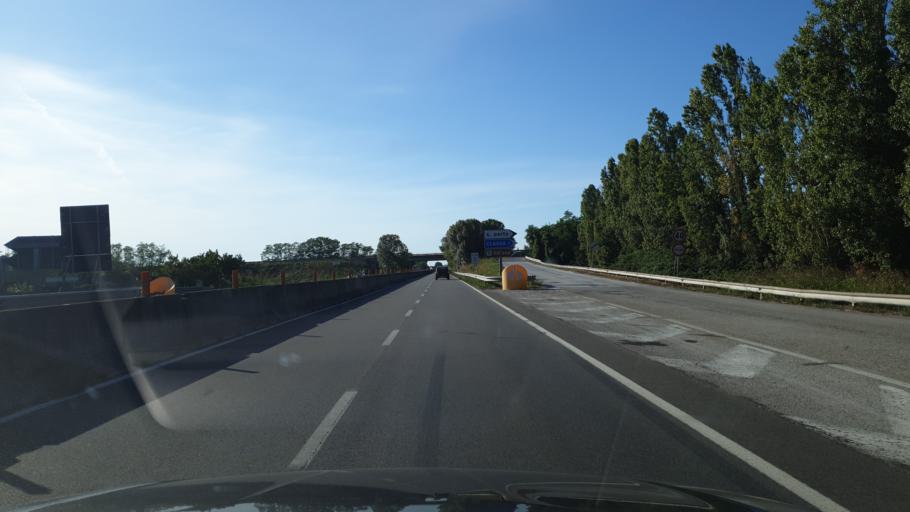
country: IT
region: Emilia-Romagna
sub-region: Provincia di Ravenna
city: Classe
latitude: 44.3711
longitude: 12.2394
